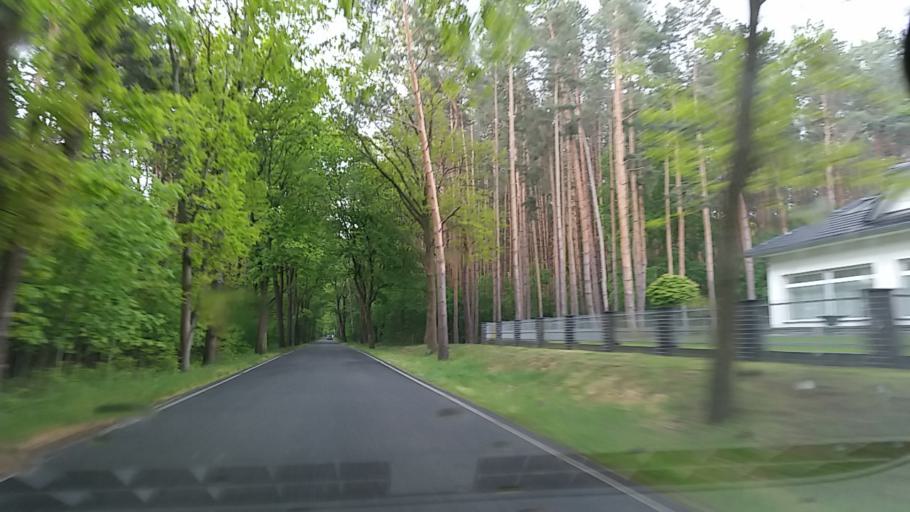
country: DE
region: Brandenburg
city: Diensdorf-Radlow
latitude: 52.2613
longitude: 14.0373
